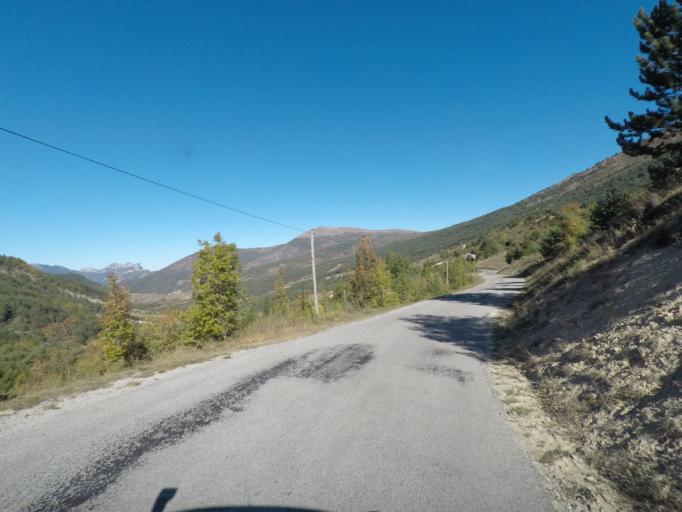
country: FR
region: Rhone-Alpes
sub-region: Departement de la Drome
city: Die
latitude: 44.5413
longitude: 5.3694
